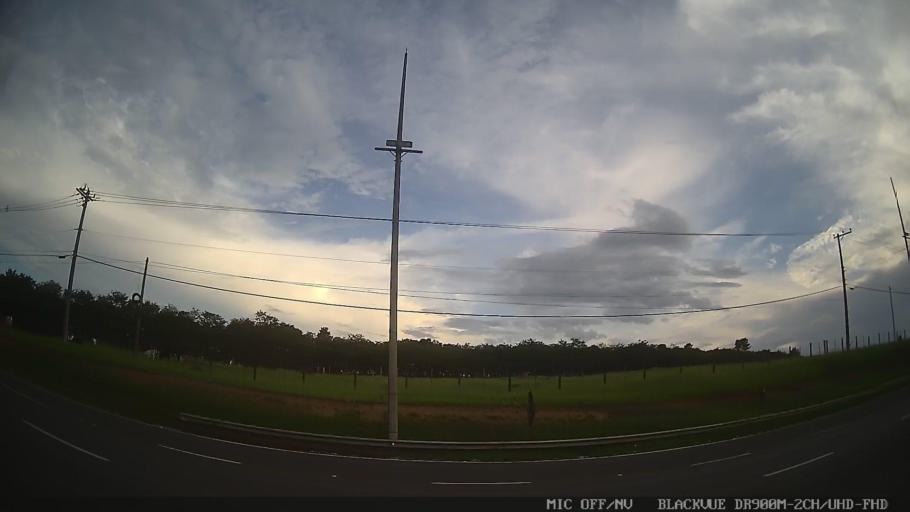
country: BR
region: Sao Paulo
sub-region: Porto Feliz
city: Porto Feliz
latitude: -23.2271
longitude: -47.5611
